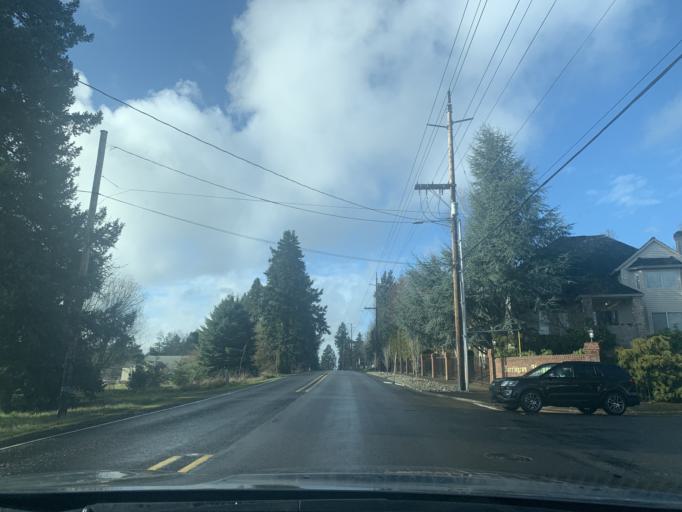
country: US
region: Oregon
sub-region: Washington County
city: King City
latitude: 45.4031
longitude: -122.8219
